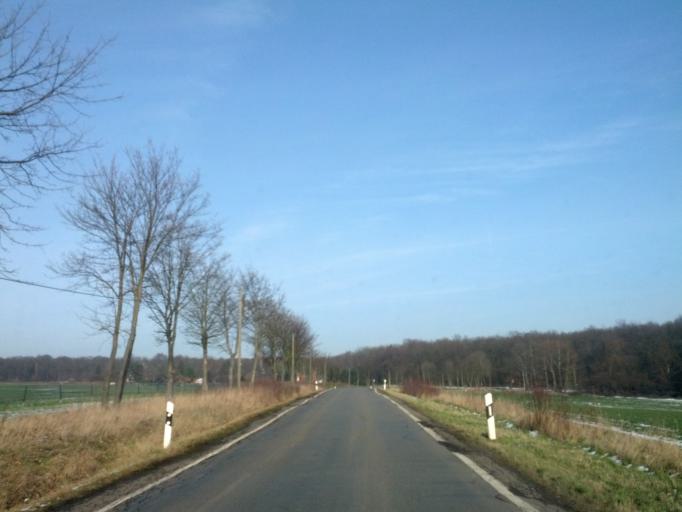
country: DE
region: Thuringia
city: Rockhausen
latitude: 50.9330
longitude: 11.0206
